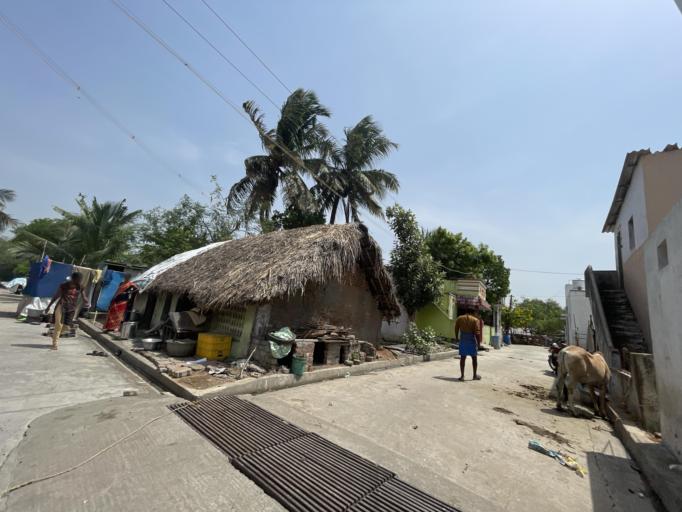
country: IN
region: Tamil Nadu
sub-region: Villupuram
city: Auroville
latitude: 11.9776
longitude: 79.7214
